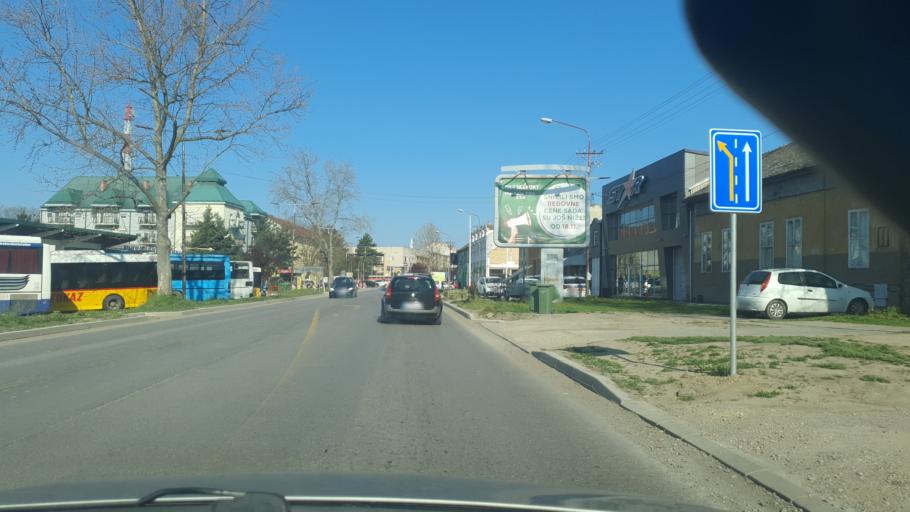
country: RS
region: Autonomna Pokrajina Vojvodina
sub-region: Zapadnobacki Okrug
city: Kula
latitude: 45.6087
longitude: 19.5351
